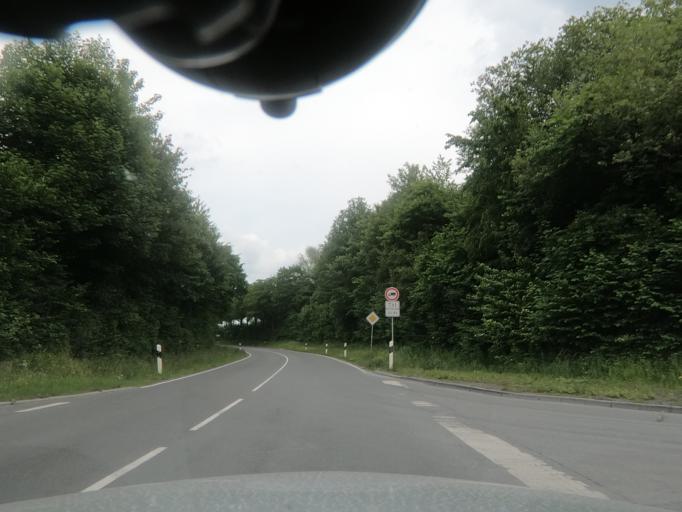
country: DE
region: North Rhine-Westphalia
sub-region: Regierungsbezirk Arnsberg
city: Ruthen
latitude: 51.4522
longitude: 8.4167
